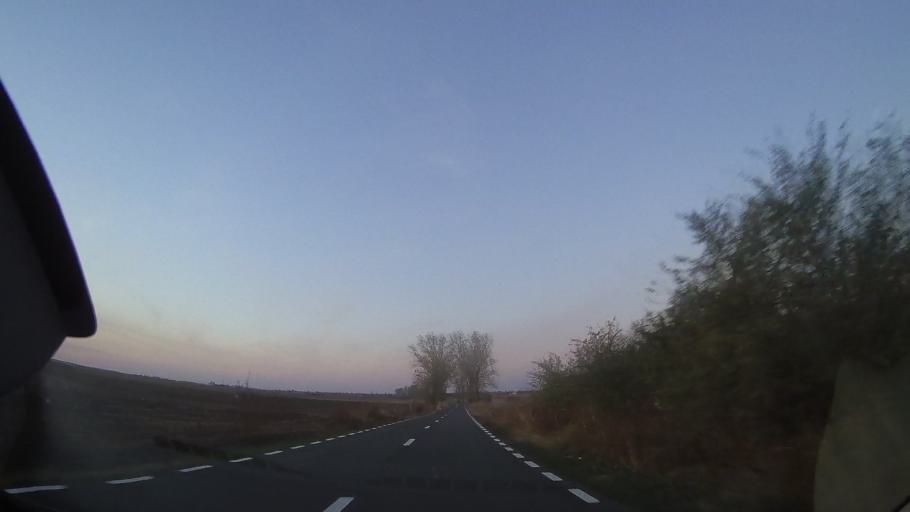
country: RO
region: Constanta
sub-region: Comuna Cobadin
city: Cobadin
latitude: 44.0375
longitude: 28.2585
